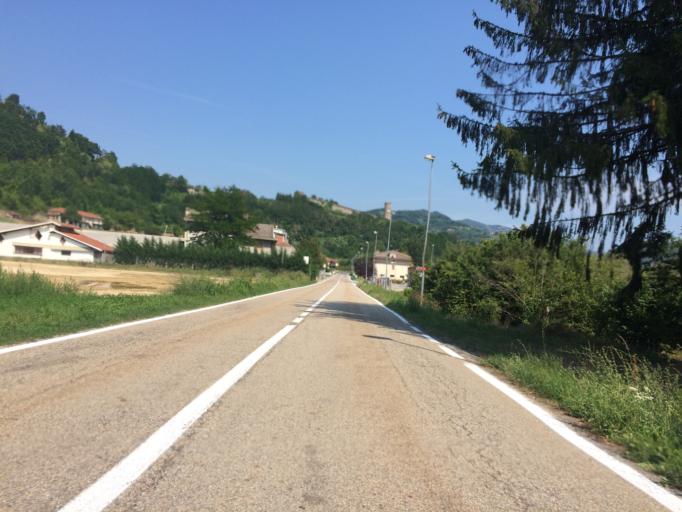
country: IT
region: Piedmont
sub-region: Provincia di Cuneo
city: Cortemilia
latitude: 44.5821
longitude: 8.1803
